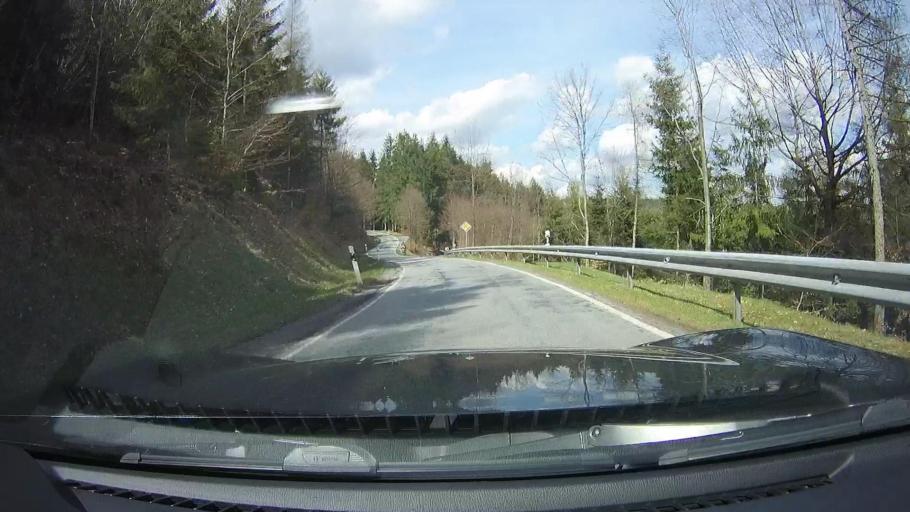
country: DE
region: Hesse
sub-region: Regierungsbezirk Darmstadt
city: Hesseneck
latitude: 49.5594
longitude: 9.1098
